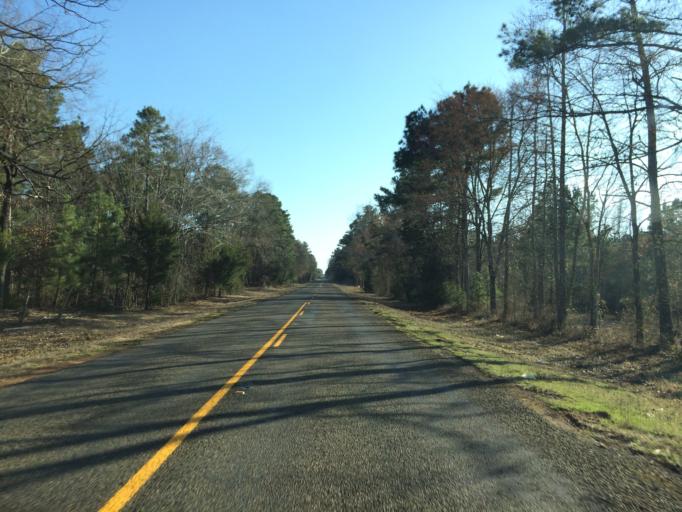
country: US
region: Texas
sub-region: Wood County
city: Hawkins
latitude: 32.6562
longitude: -95.3131
